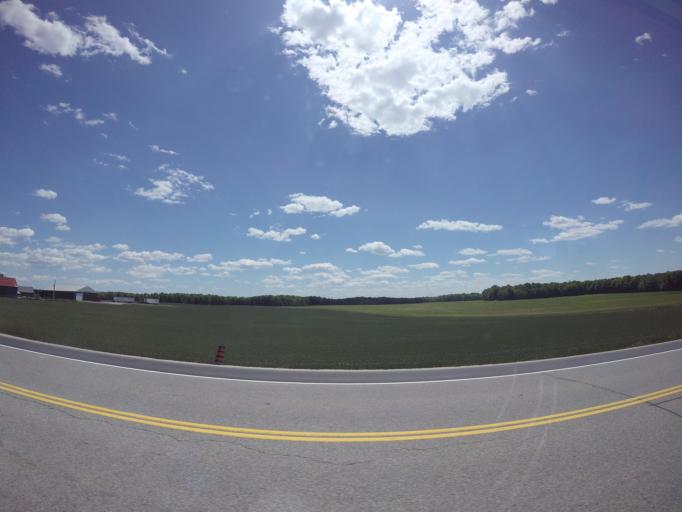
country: CA
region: Ontario
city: Carleton Place
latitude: 45.1331
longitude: -76.1944
